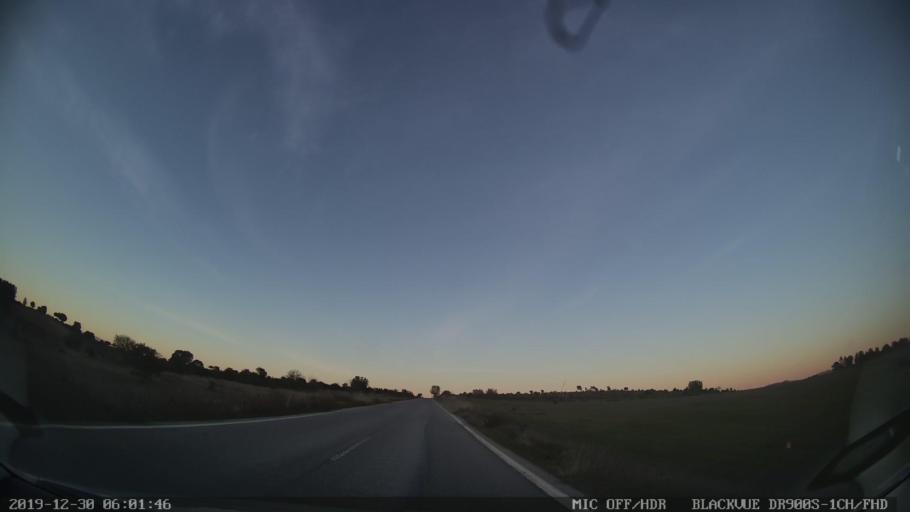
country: PT
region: Castelo Branco
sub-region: Penamacor
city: Penamacor
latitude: 40.0637
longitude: -7.2434
